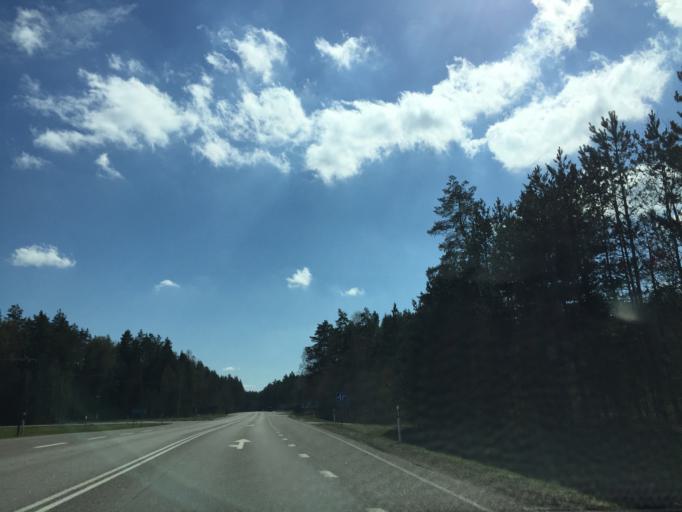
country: EE
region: Valgamaa
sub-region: Torva linn
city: Torva
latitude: 58.0127
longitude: 26.1632
